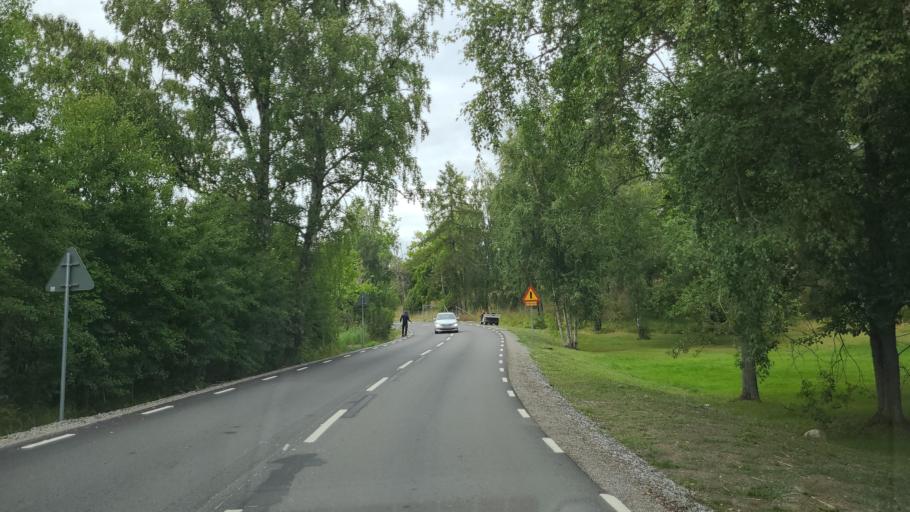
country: SE
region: Stockholm
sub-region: Upplands-Bro Kommun
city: Bro
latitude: 59.5019
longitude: 17.6257
